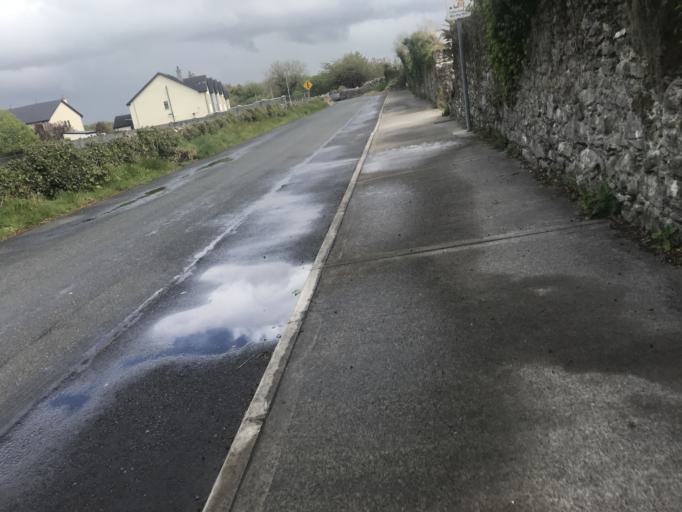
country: IE
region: Connaught
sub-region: County Galway
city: Moycullen
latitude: 53.4686
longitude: -9.1005
